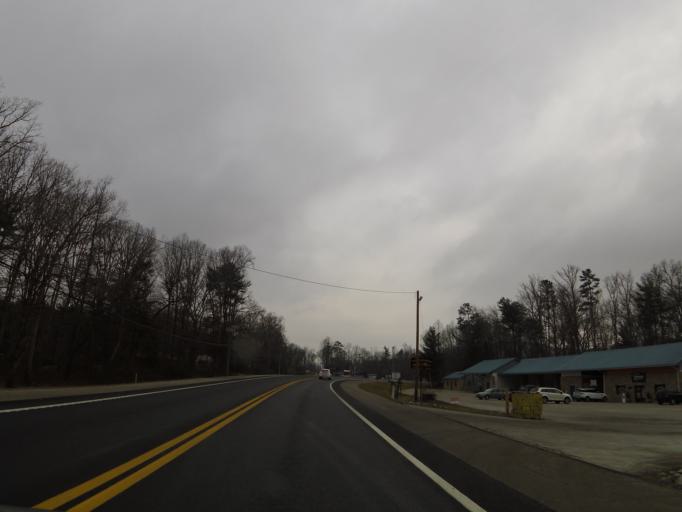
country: US
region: Tennessee
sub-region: Morgan County
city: Wartburg
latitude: 36.0977
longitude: -84.5815
